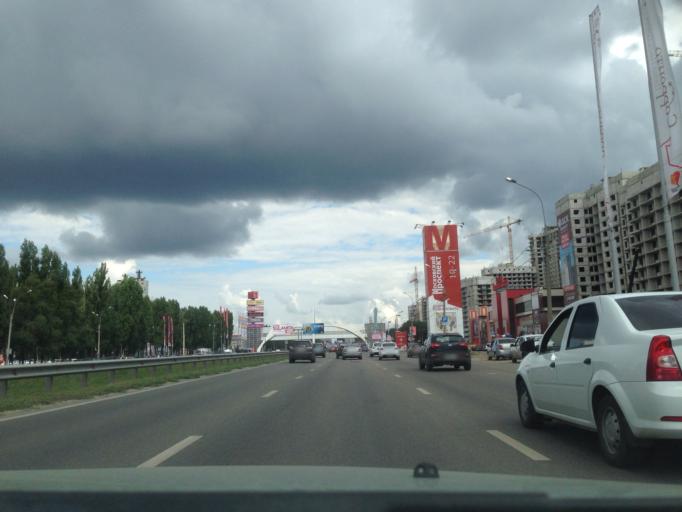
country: RU
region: Voronezj
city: Podgornoye
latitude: 51.7150
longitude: 39.1805
